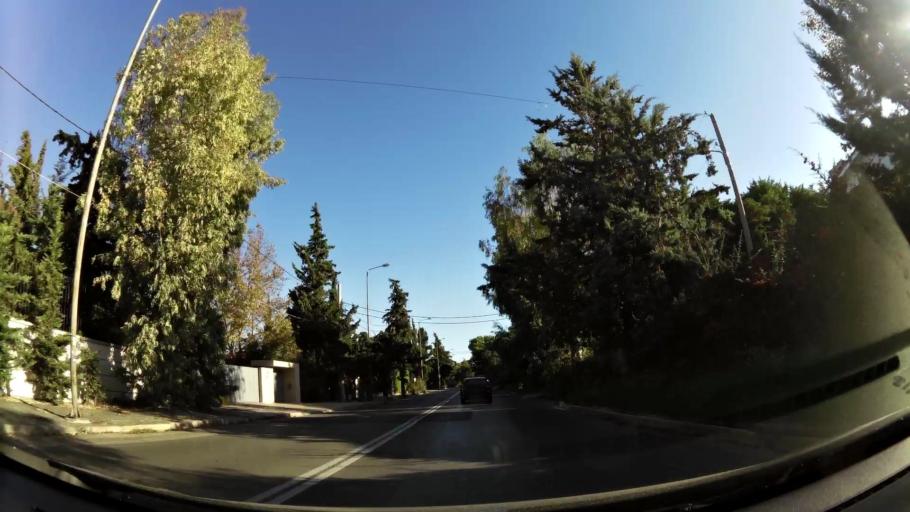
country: GR
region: Attica
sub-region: Nomarchia Athinas
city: Ekali
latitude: 38.1038
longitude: 23.8309
